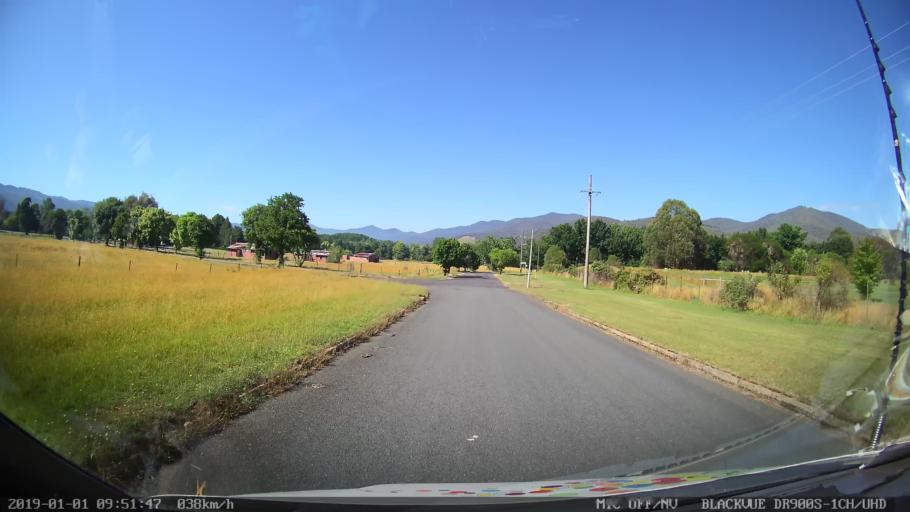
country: AU
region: New South Wales
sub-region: Snowy River
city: Jindabyne
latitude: -36.2156
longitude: 148.1228
